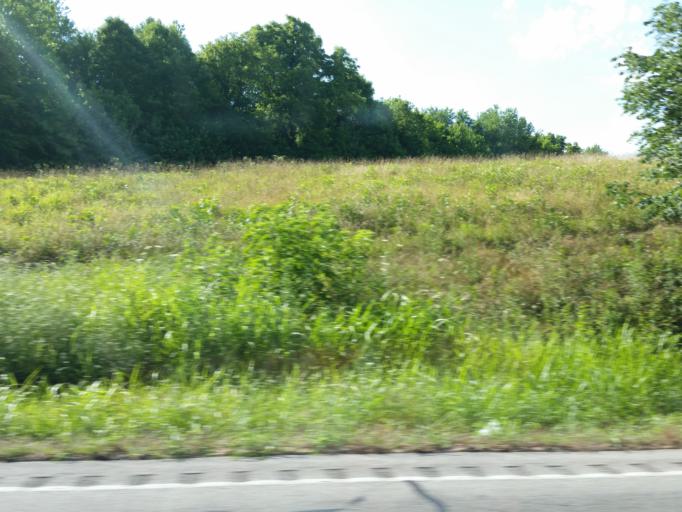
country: US
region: Tennessee
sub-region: Perry County
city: Linden
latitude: 35.6250
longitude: -87.8158
